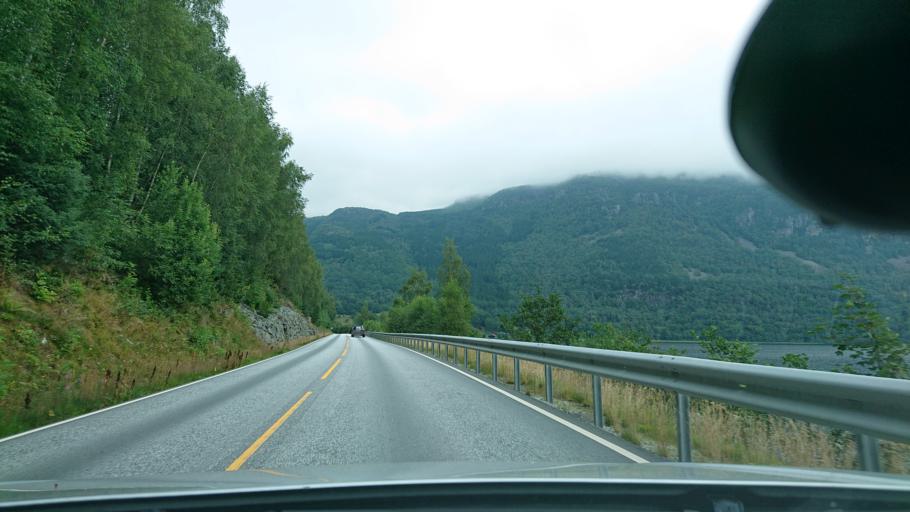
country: NO
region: Rogaland
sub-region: Hjelmeland
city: Hjelmelandsvagen
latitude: 59.1564
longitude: 6.1739
